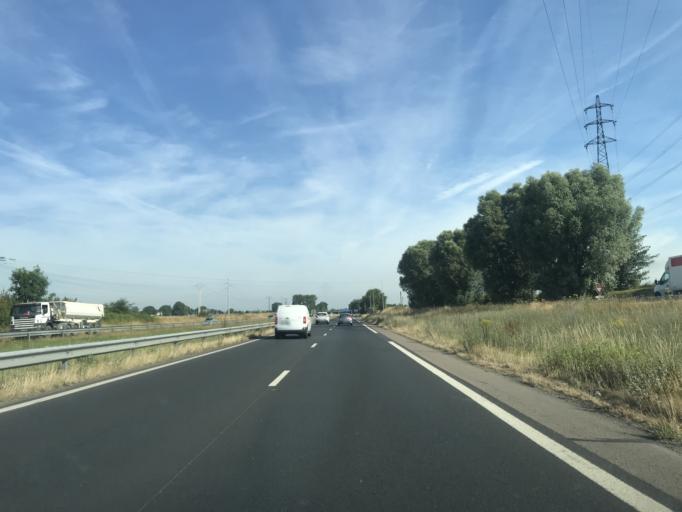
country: FR
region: Haute-Normandie
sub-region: Departement de la Seine-Maritime
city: La Vaupaliere
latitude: 49.4958
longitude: 0.9967
